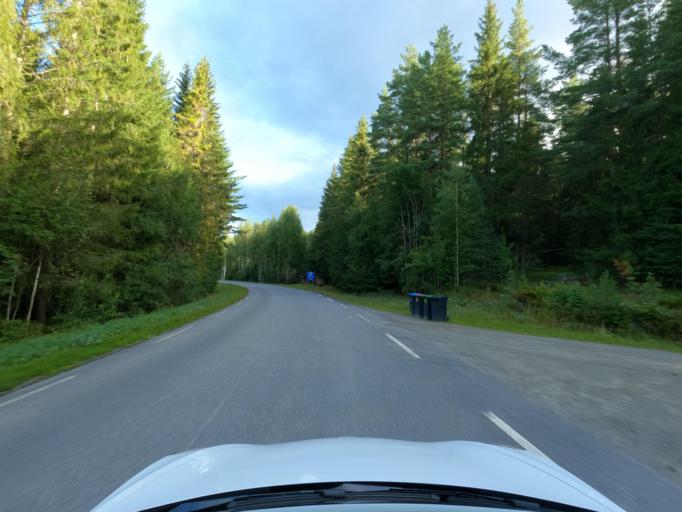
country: NO
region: Telemark
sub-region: Hjartdal
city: Sauland
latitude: 59.7880
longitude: 9.1035
